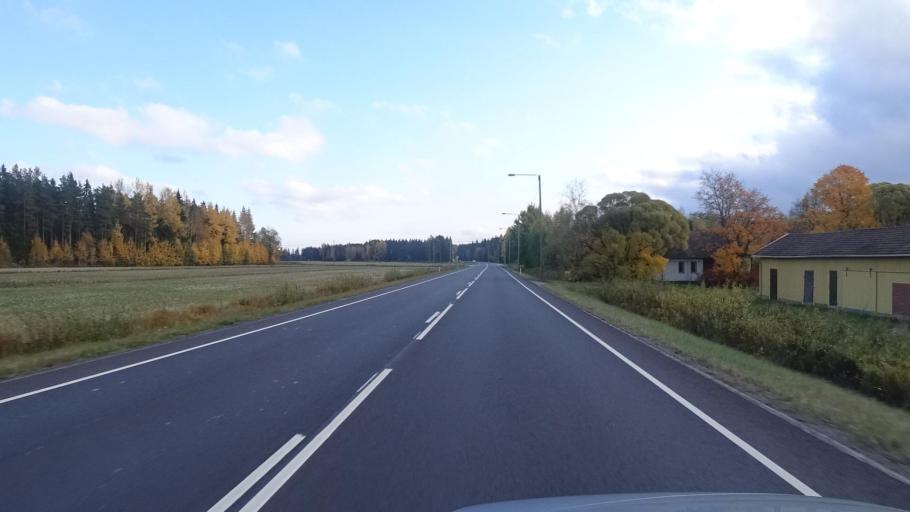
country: FI
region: Satakunta
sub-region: Rauma
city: Koeylioe
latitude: 61.0984
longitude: 22.2367
